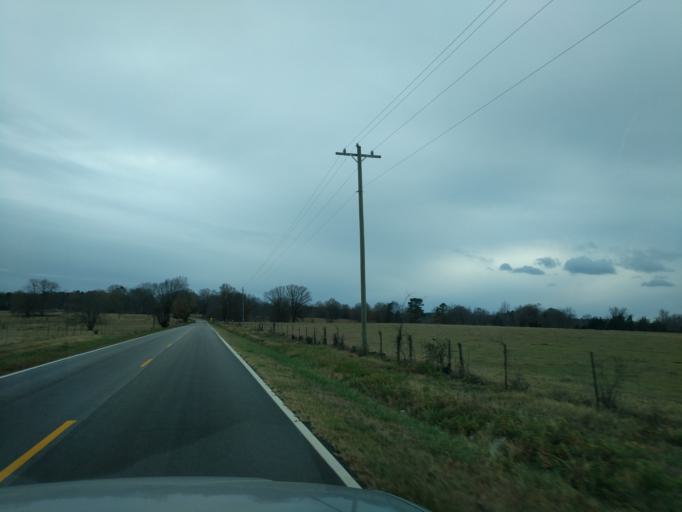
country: US
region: South Carolina
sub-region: Laurens County
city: Laurens
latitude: 34.3522
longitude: -81.9909
